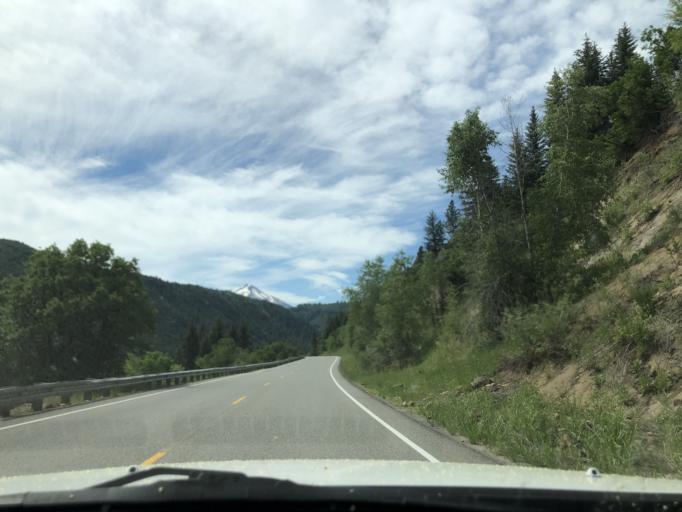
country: US
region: Colorado
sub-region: Delta County
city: Paonia
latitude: 38.9758
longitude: -107.3427
